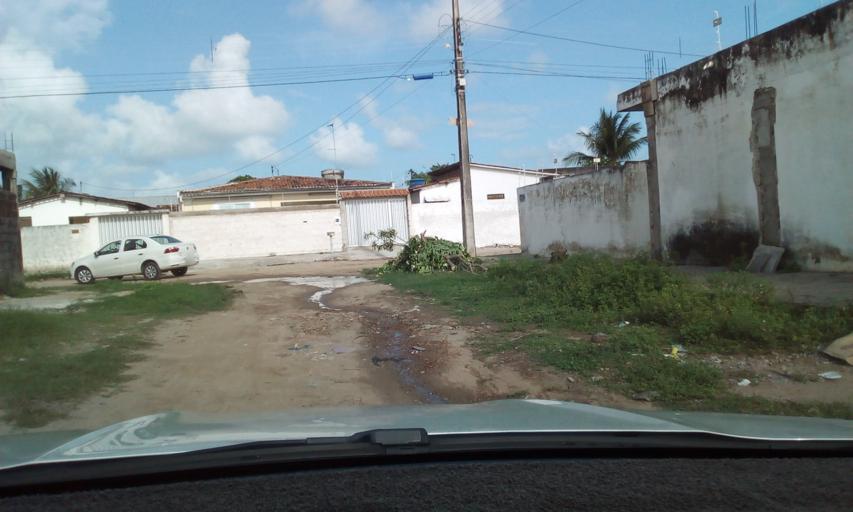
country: BR
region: Paraiba
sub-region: Joao Pessoa
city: Joao Pessoa
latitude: -7.1834
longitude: -34.8262
